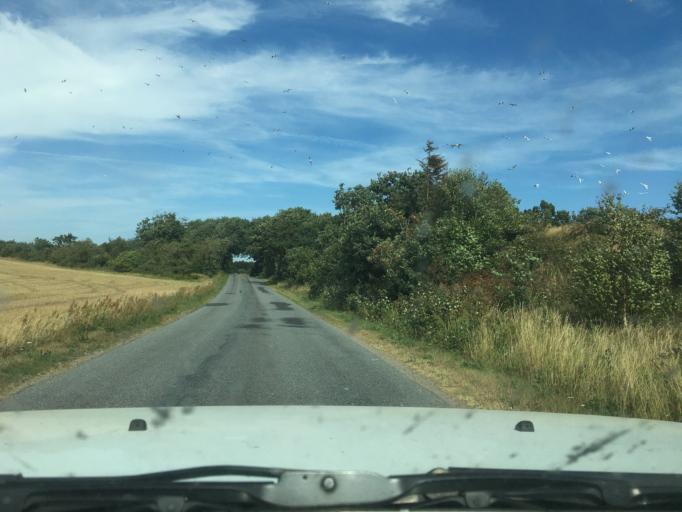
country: DK
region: North Denmark
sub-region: Vesthimmerland Kommune
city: Farso
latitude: 56.6319
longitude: 9.3580
